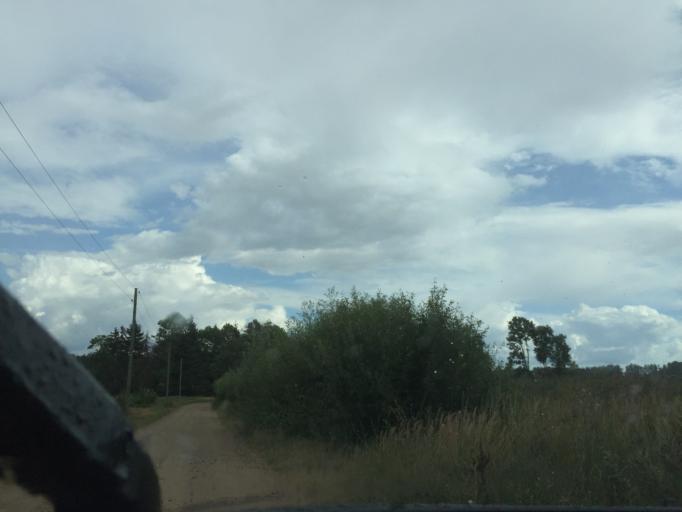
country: LT
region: Siauliu apskritis
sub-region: Joniskis
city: Joniskis
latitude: 56.3437
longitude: 23.5503
